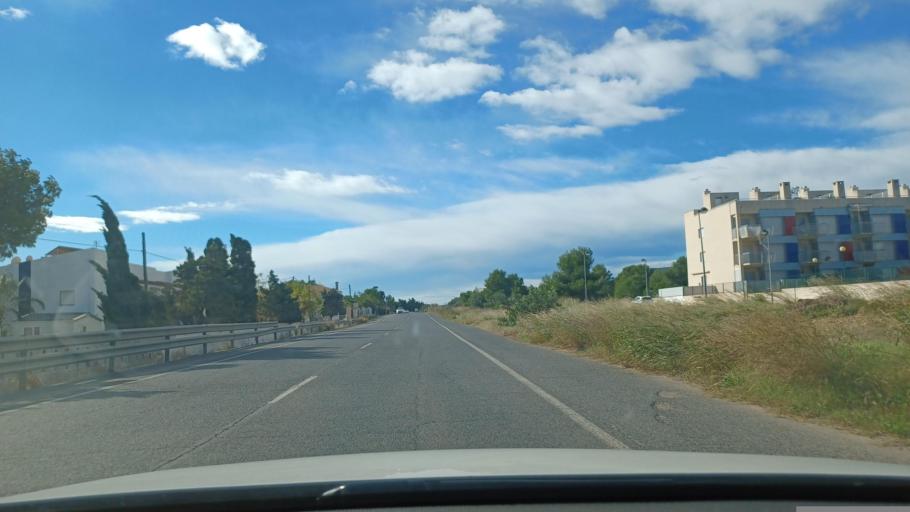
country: ES
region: Catalonia
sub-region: Provincia de Tarragona
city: Sant Carles de la Rapita
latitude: 40.5942
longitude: 0.5688
